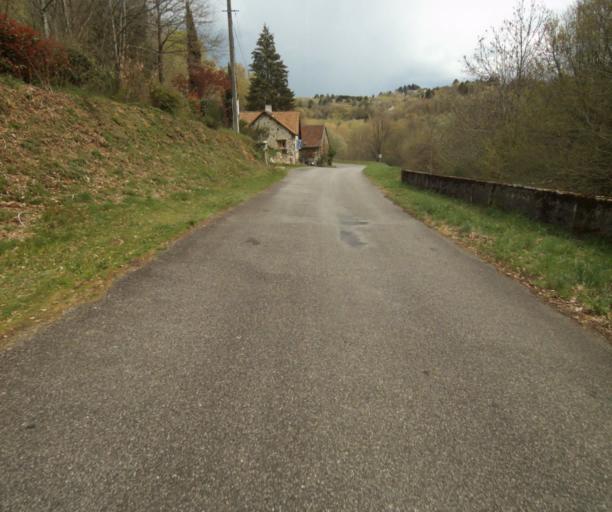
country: FR
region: Limousin
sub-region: Departement de la Correze
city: Naves
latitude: 45.3092
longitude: 1.7985
